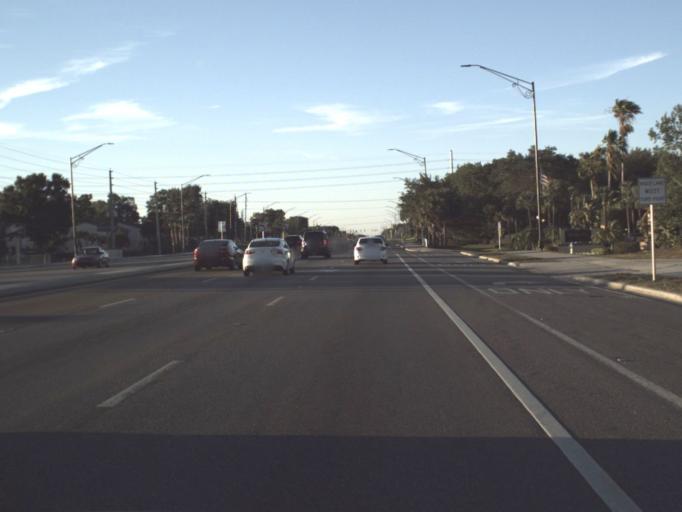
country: US
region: Florida
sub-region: Orange County
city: Conway
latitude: 28.4998
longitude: -81.3101
